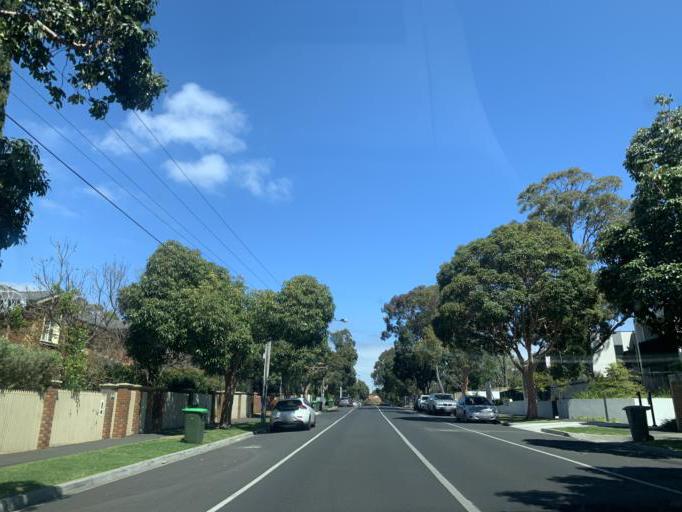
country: AU
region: Victoria
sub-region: Bayside
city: Brighton East
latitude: -37.9060
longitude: 145.0146
